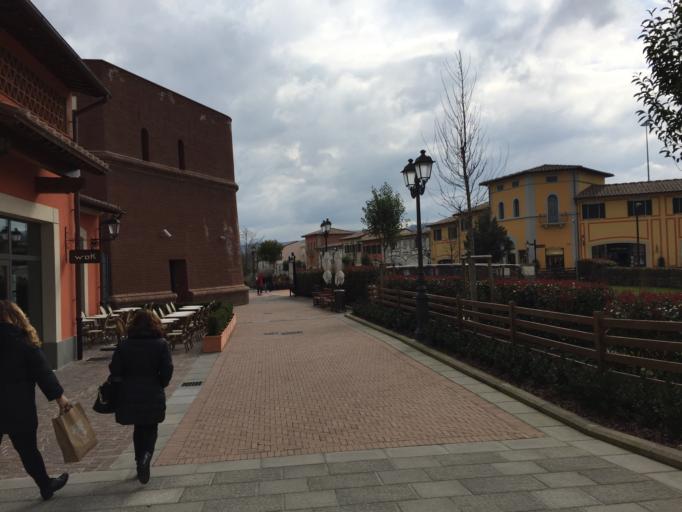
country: IT
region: Tuscany
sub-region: Province of Florence
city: Cavallina
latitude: 43.9855
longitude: 11.2142
